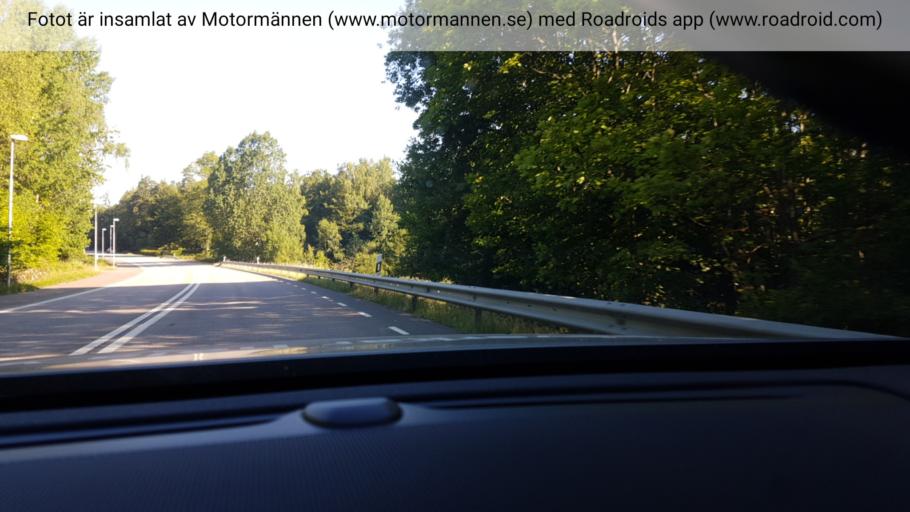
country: SE
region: Skane
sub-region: Hassleholms Kommun
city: Bjarnum
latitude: 56.3269
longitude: 13.6810
